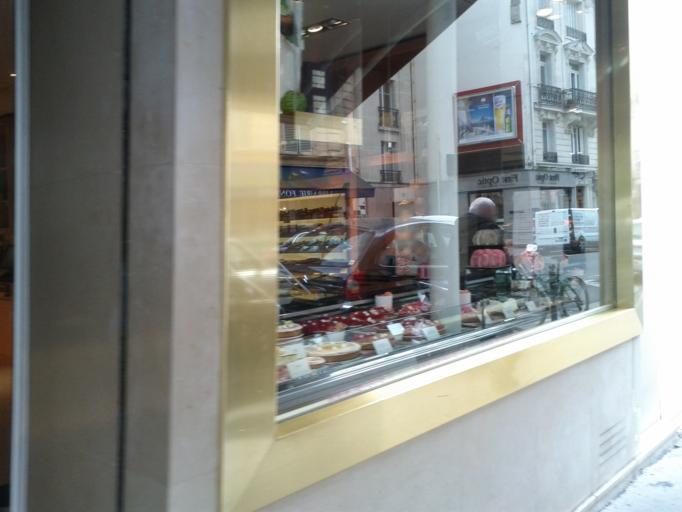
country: FR
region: Ile-de-France
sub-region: Departement des Hauts-de-Seine
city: Boulogne-Billancourt
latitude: 48.8478
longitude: 2.2652
